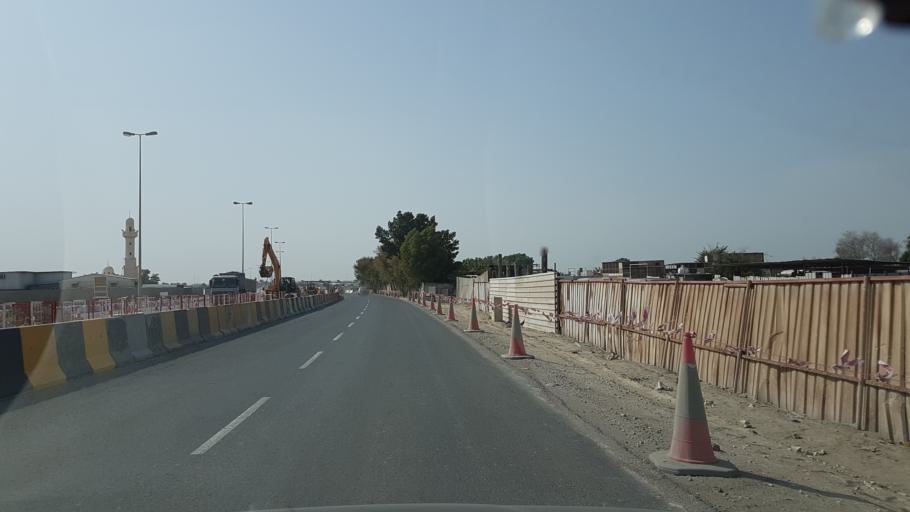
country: BH
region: Northern
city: Madinat `Isa
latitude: 26.1658
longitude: 50.5132
